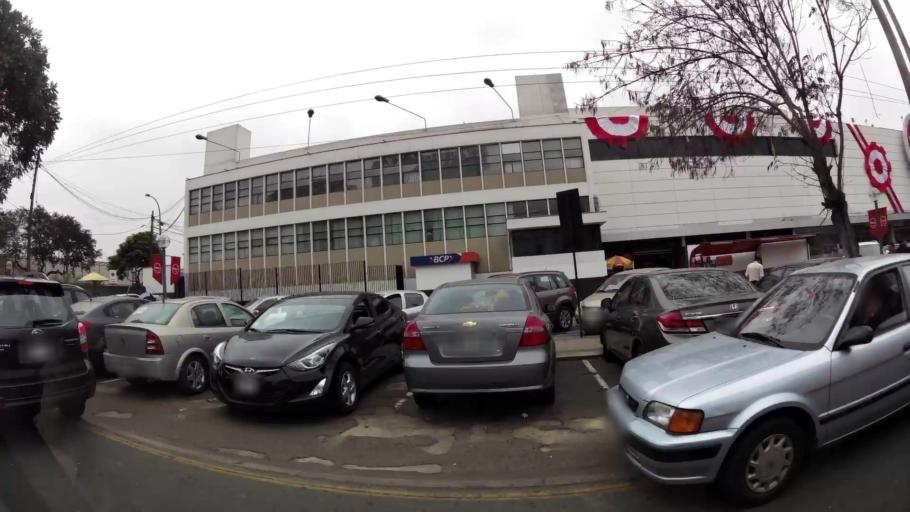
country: PE
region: Lima
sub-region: Lima
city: Surco
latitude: -12.1256
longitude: -77.0181
